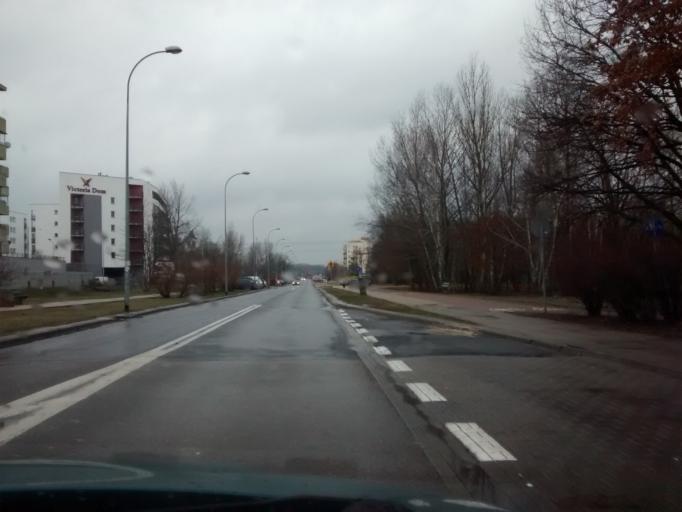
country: PL
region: Masovian Voivodeship
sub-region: Warszawa
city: Bialoleka
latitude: 52.3242
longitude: 20.9597
